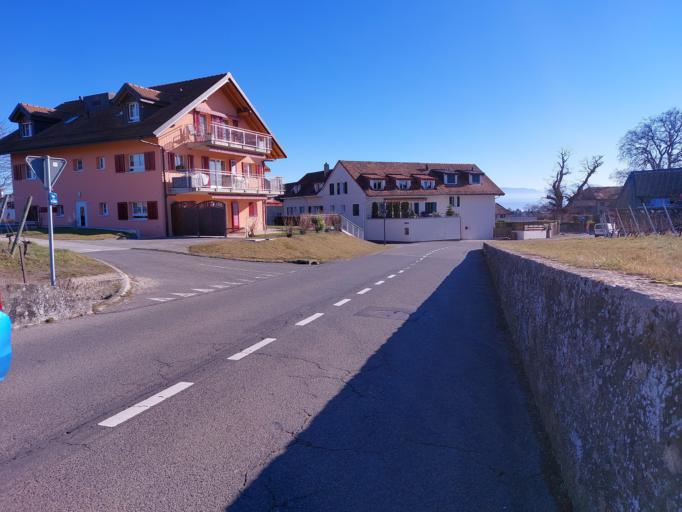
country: CH
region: Vaud
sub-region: Morges District
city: Morges
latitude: 46.5209
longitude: 6.4768
